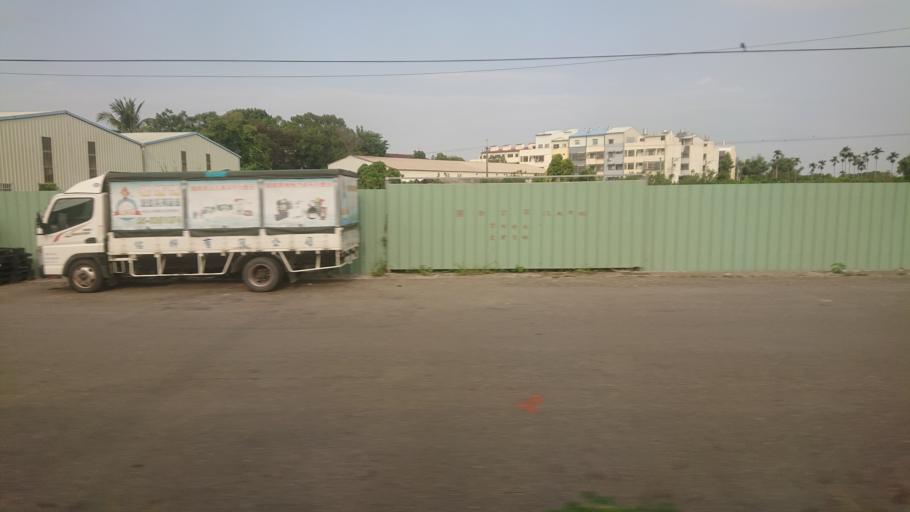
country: TW
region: Taiwan
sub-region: Yunlin
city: Douliu
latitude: 23.7173
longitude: 120.5652
